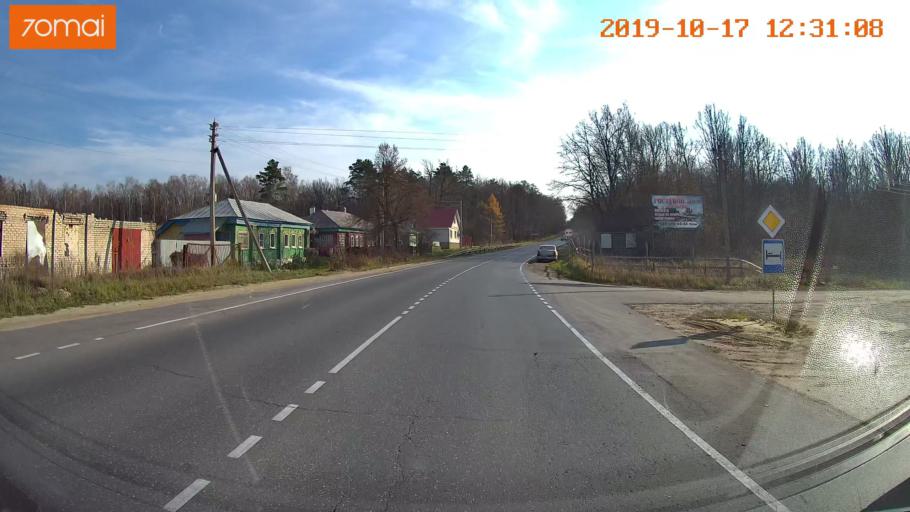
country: RU
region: Rjazan
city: Syntul
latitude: 54.9709
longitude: 41.3302
